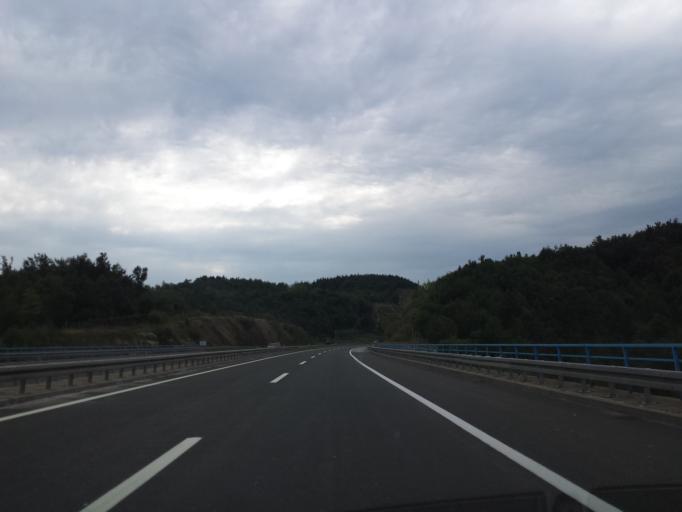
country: HR
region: Karlovacka
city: Ostarije
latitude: 45.1504
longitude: 15.2731
